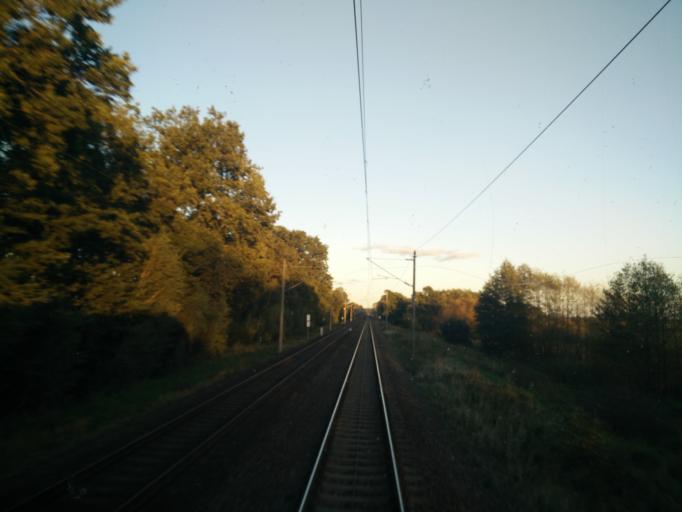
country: DE
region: Brandenburg
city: Breese
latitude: 52.9907
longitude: 11.8246
